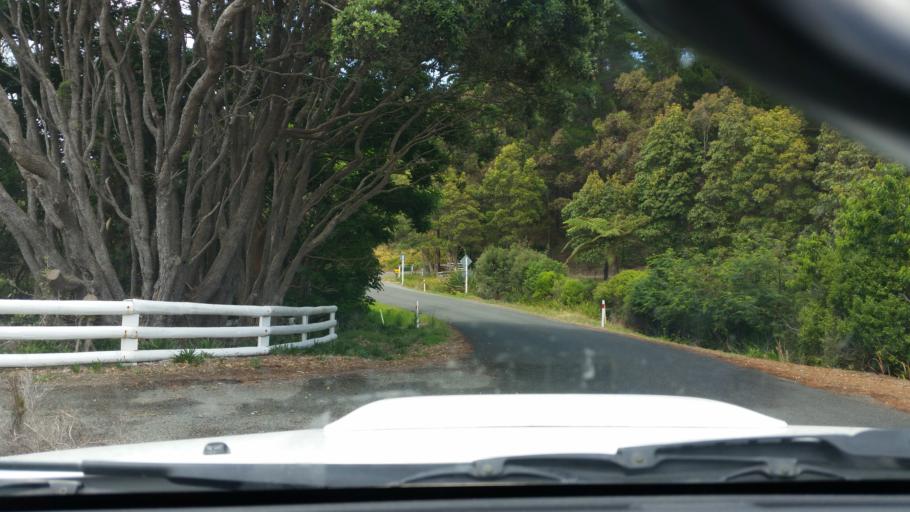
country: NZ
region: Northland
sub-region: Kaipara District
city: Dargaville
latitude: -35.7984
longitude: 173.6236
